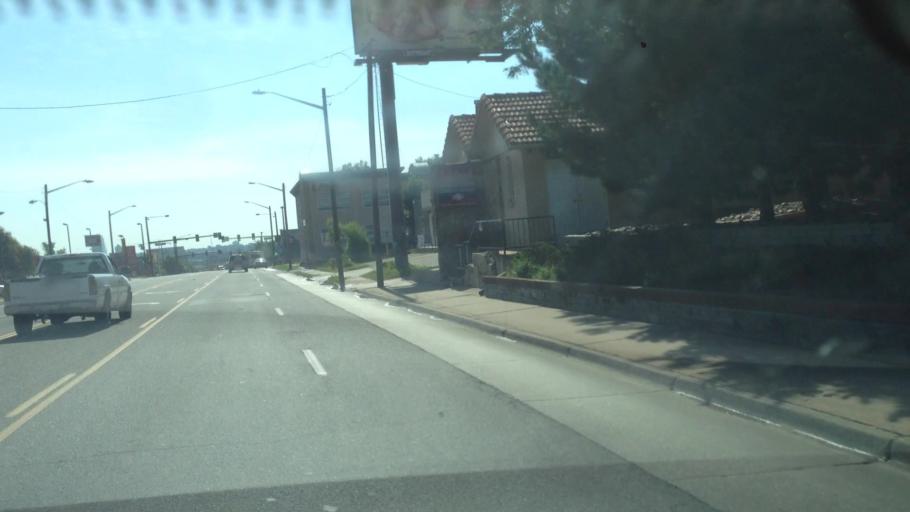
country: US
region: Colorado
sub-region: Denver County
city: Denver
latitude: 39.7111
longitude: -105.0180
